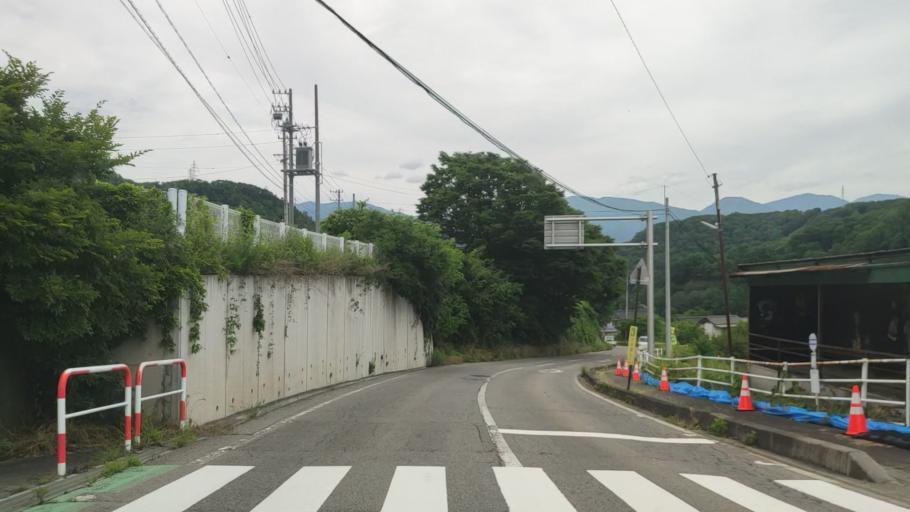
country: JP
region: Nagano
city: Kamimaruko
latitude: 36.3278
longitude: 138.3436
